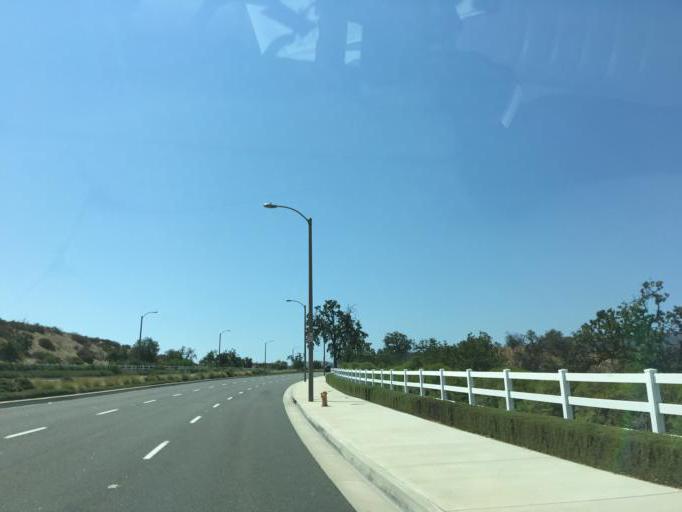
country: US
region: California
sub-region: Los Angeles County
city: Santa Clarita
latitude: 34.3981
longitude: -118.5751
